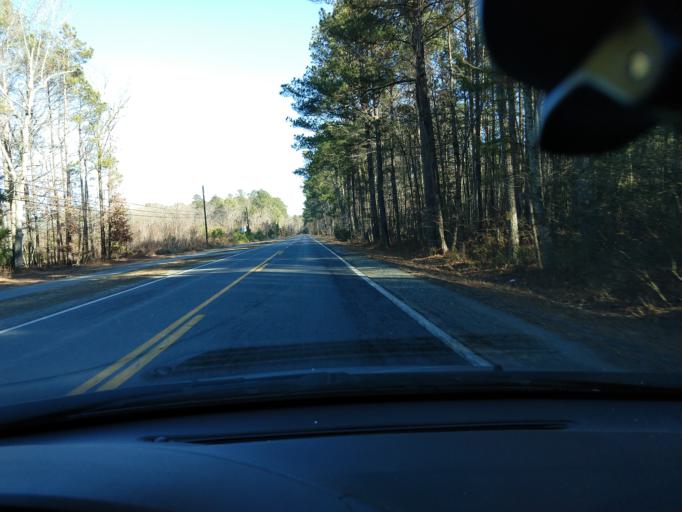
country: US
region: Virginia
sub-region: Charles City County
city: Charles City
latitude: 37.3260
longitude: -76.9942
